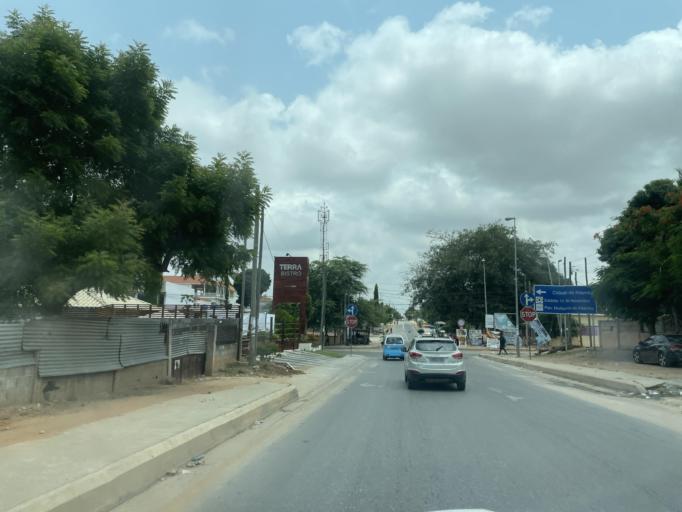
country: AO
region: Luanda
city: Luanda
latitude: -8.9389
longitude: 13.1687
